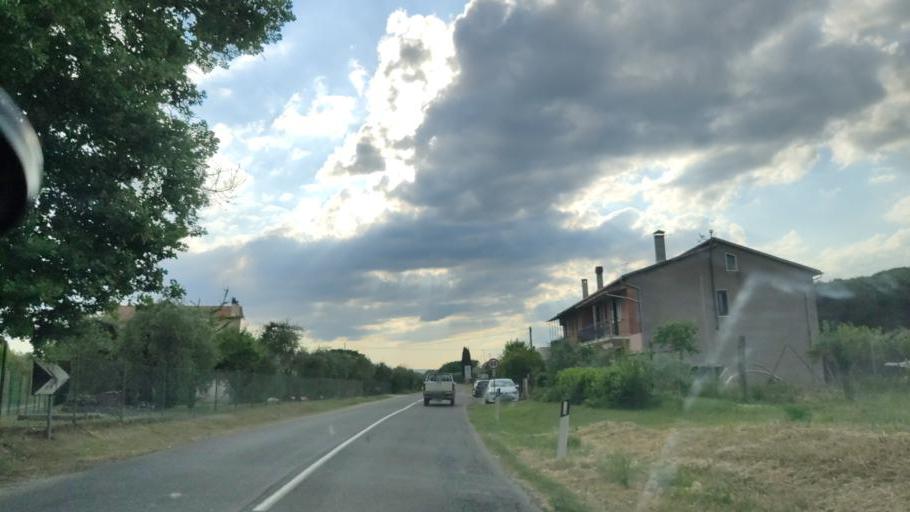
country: IT
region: Umbria
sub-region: Provincia di Terni
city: Giove
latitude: 42.5124
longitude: 12.3444
